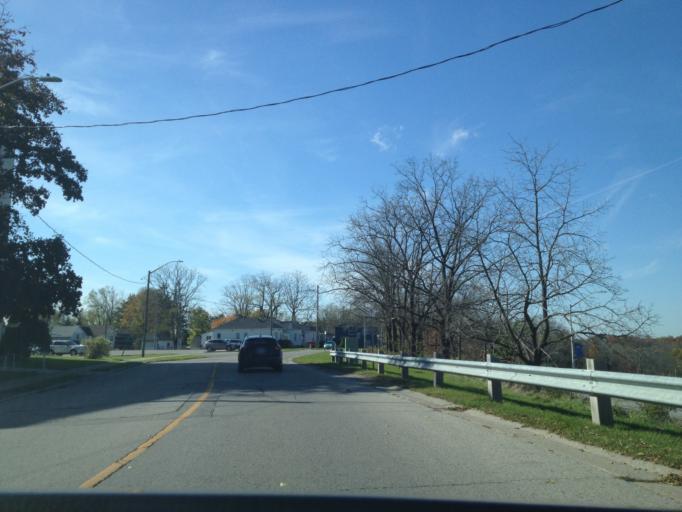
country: CA
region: Ontario
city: St. Thomas
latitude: 42.7789
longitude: -81.2047
